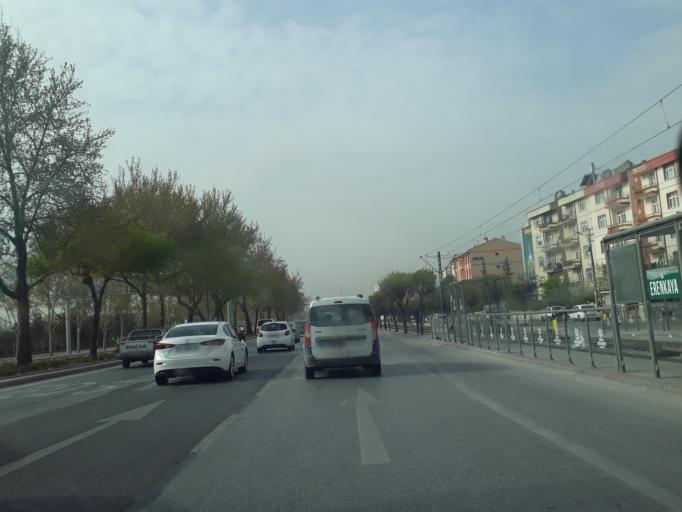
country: TR
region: Konya
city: Selcuklu
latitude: 37.9441
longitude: 32.5120
